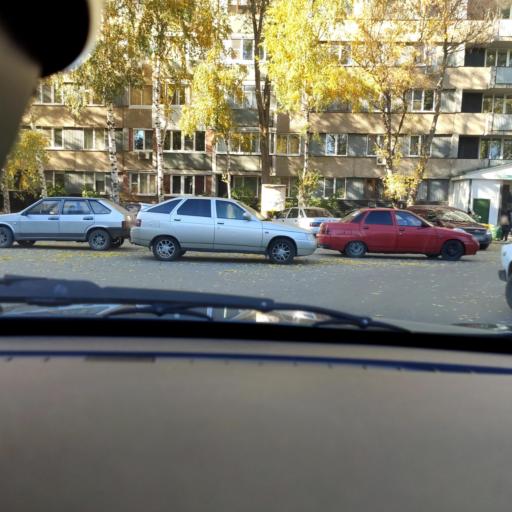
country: RU
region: Samara
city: Tol'yatti
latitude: 53.5171
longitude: 49.2897
